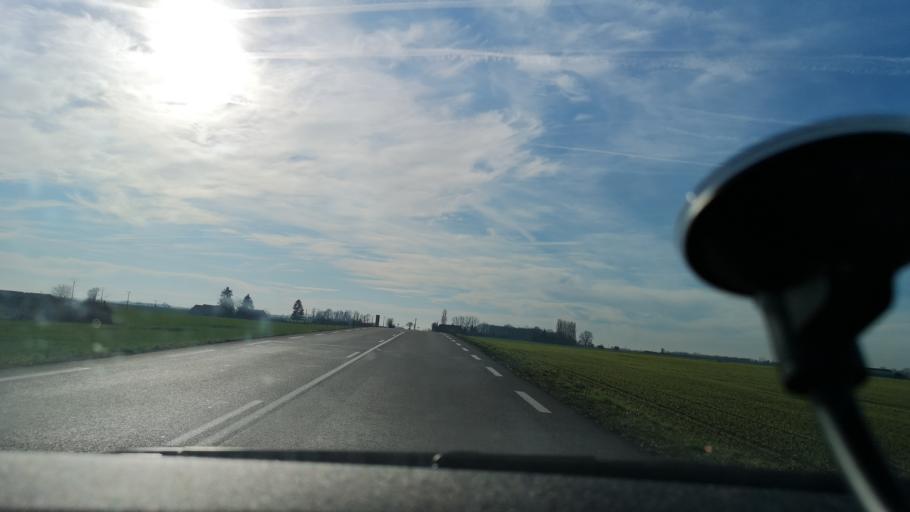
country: FR
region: Bourgogne
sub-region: Departement de la Cote-d'Or
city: Seurre
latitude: 46.9581
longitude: 5.1666
